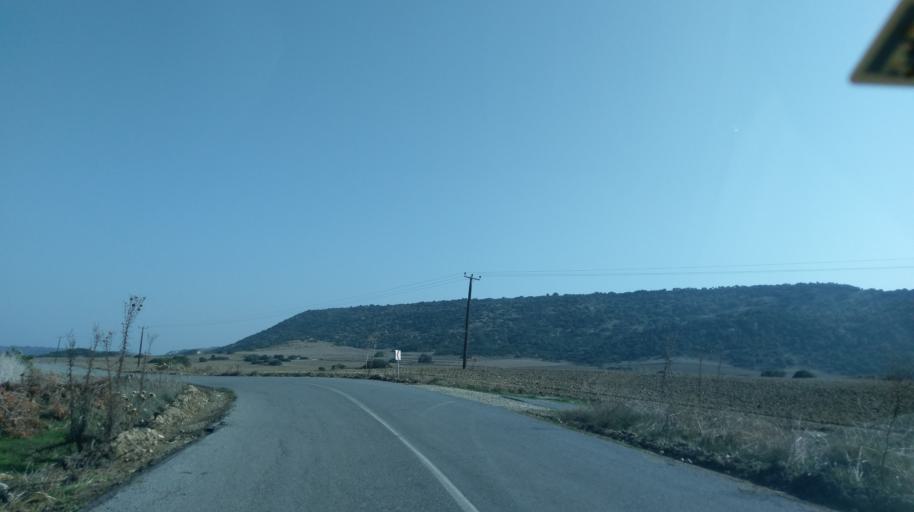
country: CY
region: Ammochostos
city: Leonarisso
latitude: 35.5064
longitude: 34.2566
